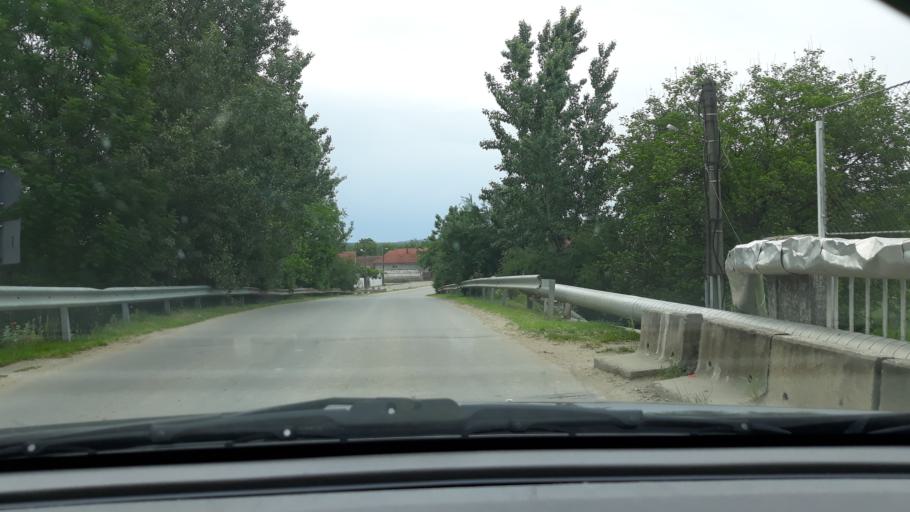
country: RO
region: Bihor
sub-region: Comuna Osorheiu
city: Osorheiu
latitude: 47.0600
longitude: 22.0428
